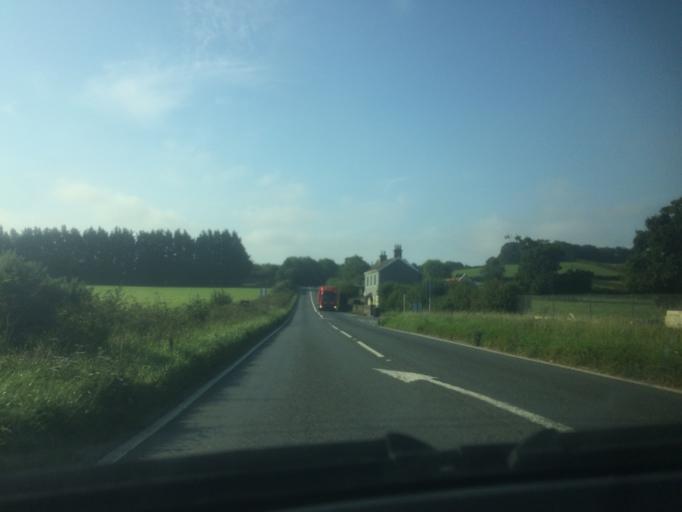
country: GB
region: England
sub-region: Cornwall
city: Pillaton
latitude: 50.4452
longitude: -4.2561
